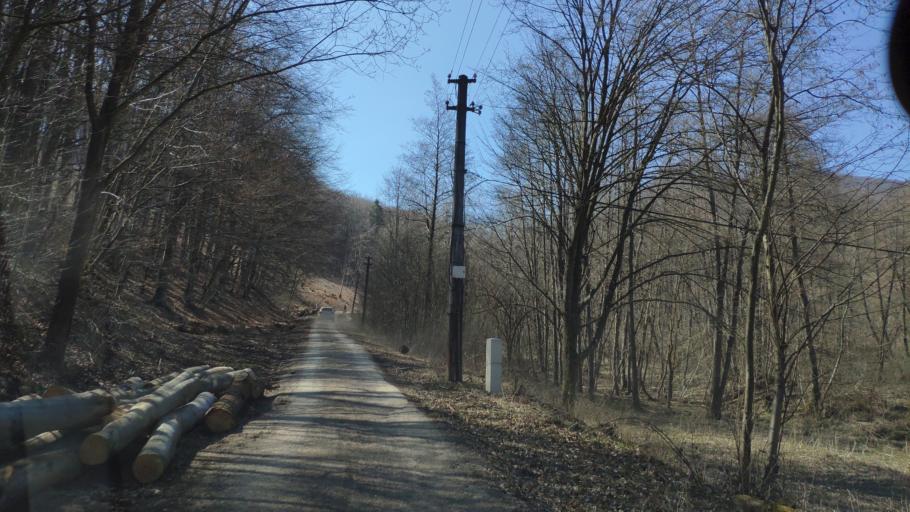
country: SK
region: Kosicky
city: Medzev
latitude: 48.6774
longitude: 20.8803
